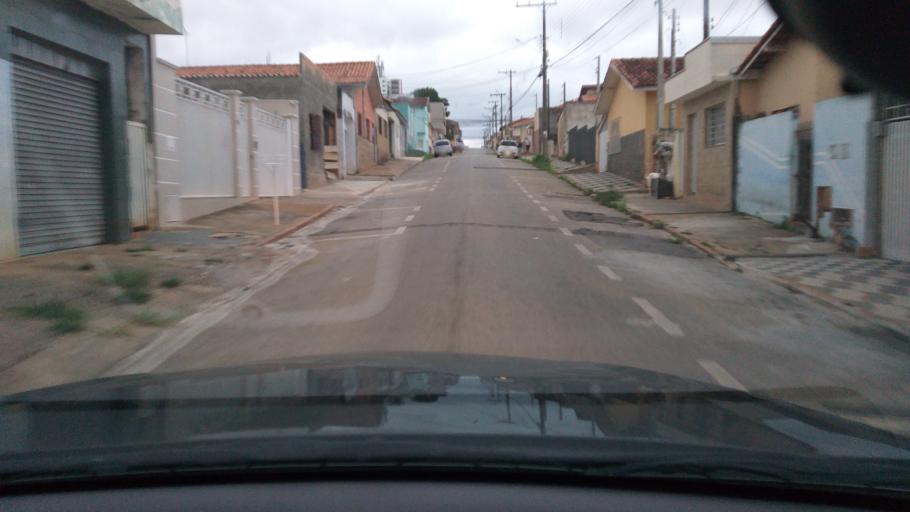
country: BR
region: Sao Paulo
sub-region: Itapeva
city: Itapeva
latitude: -23.9871
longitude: -48.8725
